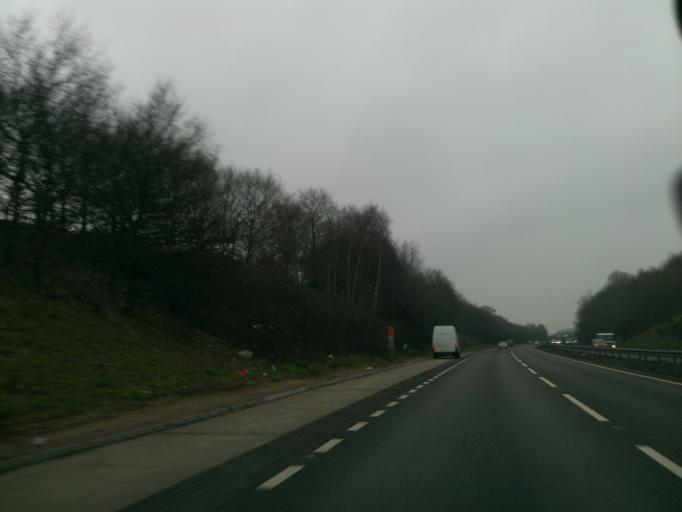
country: GB
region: England
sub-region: Essex
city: Great Horkesley
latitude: 51.9171
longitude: 0.8760
